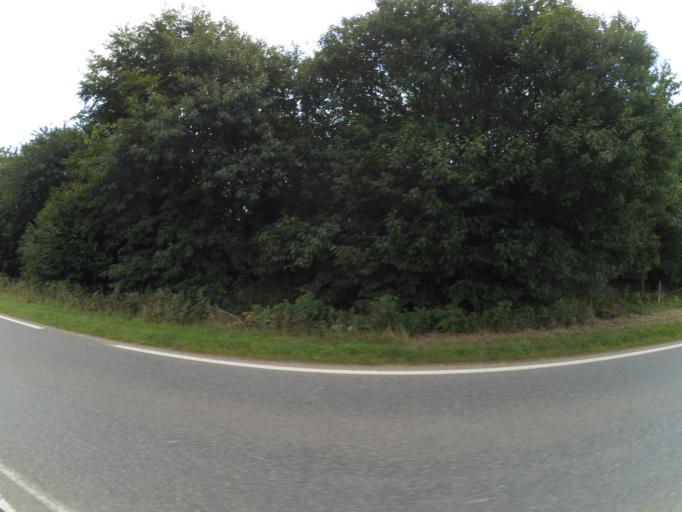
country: FR
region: Brittany
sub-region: Departement du Finistere
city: Elliant
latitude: 47.9667
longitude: -3.8691
